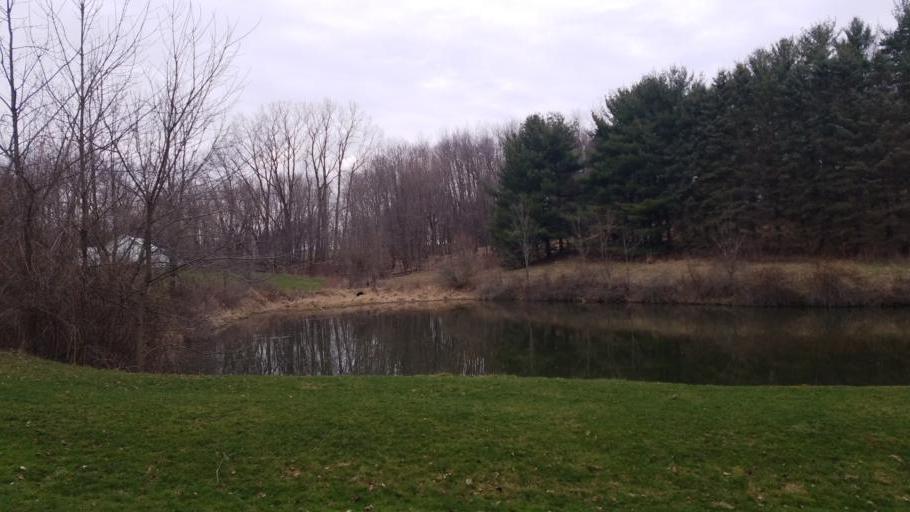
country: US
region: Ohio
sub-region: Sandusky County
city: Bellville
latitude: 40.6835
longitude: -82.4936
